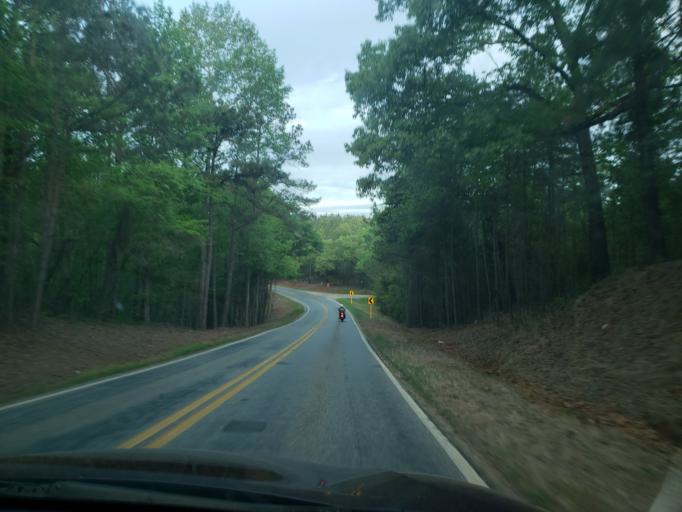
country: US
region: Alabama
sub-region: Tallapoosa County
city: Dadeville
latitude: 32.7069
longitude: -85.8215
